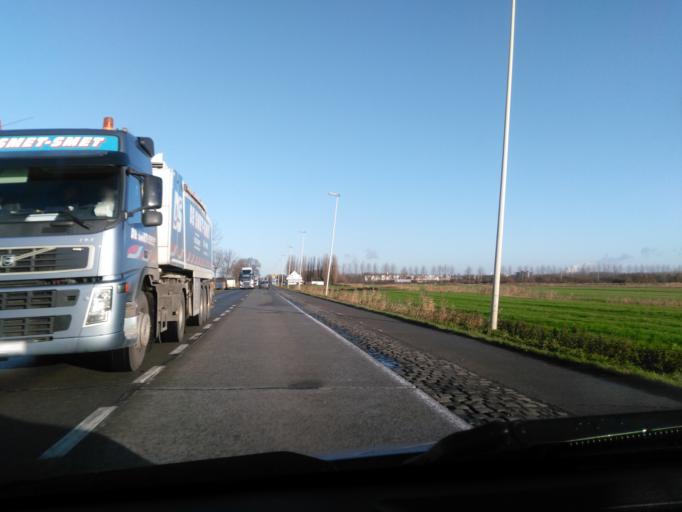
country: BE
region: Flanders
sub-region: Provincie Oost-Vlaanderen
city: Sint-Gillis-Waas
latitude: 51.2427
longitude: 4.1900
